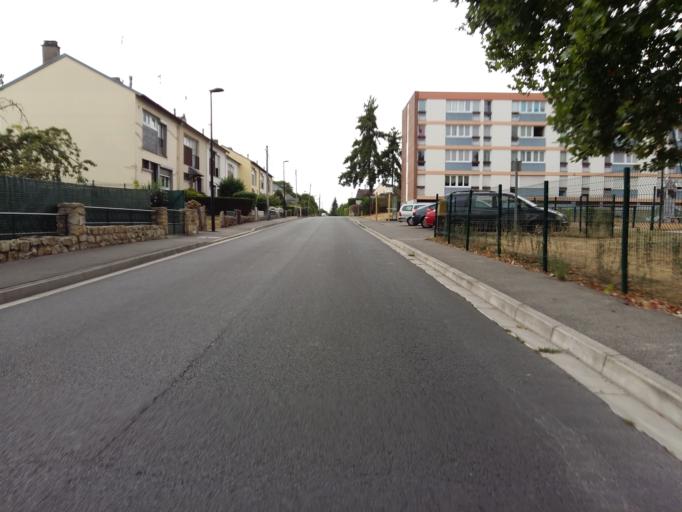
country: FR
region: Picardie
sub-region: Departement de la Somme
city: Camon
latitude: 49.8960
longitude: 2.3393
